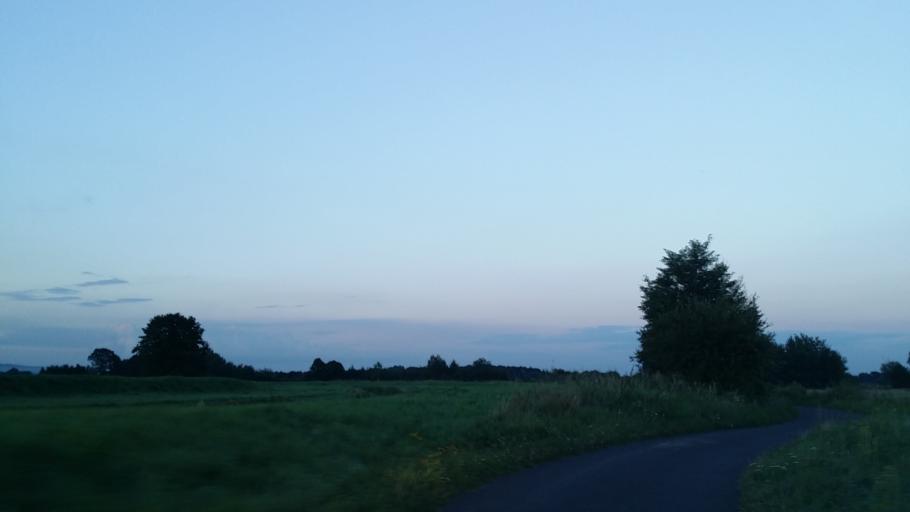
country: PL
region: Lesser Poland Voivodeship
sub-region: Powiat oswiecimski
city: Przeciszow
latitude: 50.0163
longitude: 19.3815
